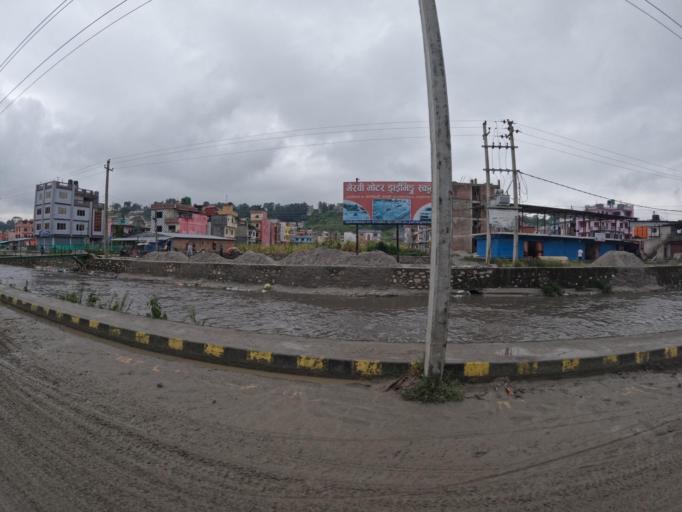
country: NP
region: Central Region
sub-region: Bagmati Zone
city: Kathmandu
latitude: 27.7551
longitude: 85.3173
